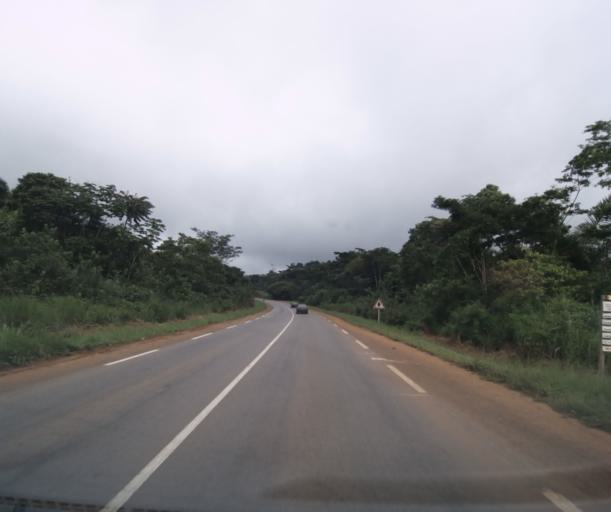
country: CM
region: Centre
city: Mbankomo
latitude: 3.7819
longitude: 11.2706
